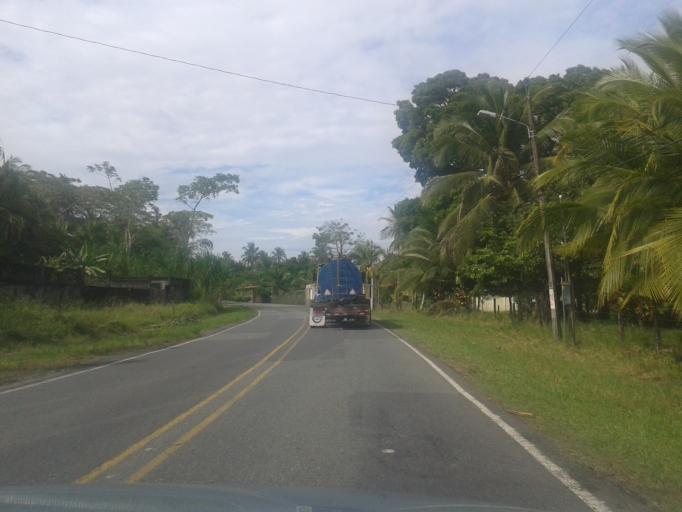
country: CR
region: Limon
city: Limon
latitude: 9.9329
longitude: -83.0039
